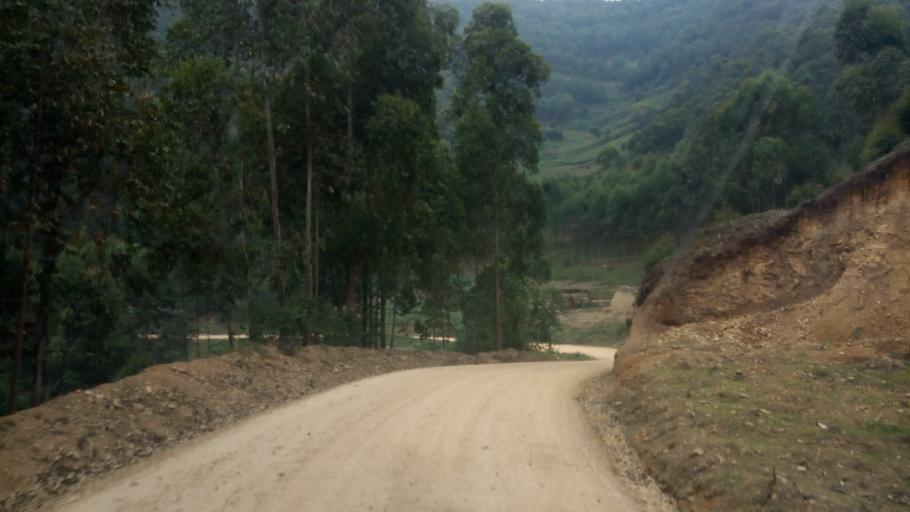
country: UG
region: Western Region
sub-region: Kanungu District
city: Kanungu
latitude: -1.1019
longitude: 29.8552
